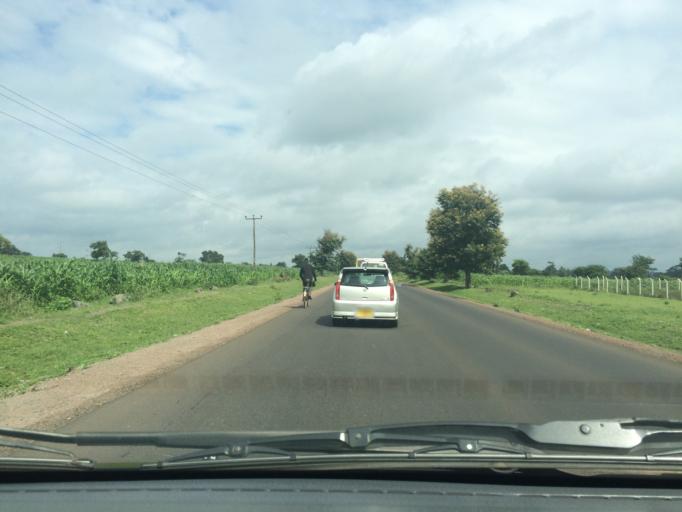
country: TZ
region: Arusha
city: Usa River
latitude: -3.3880
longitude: 36.9554
